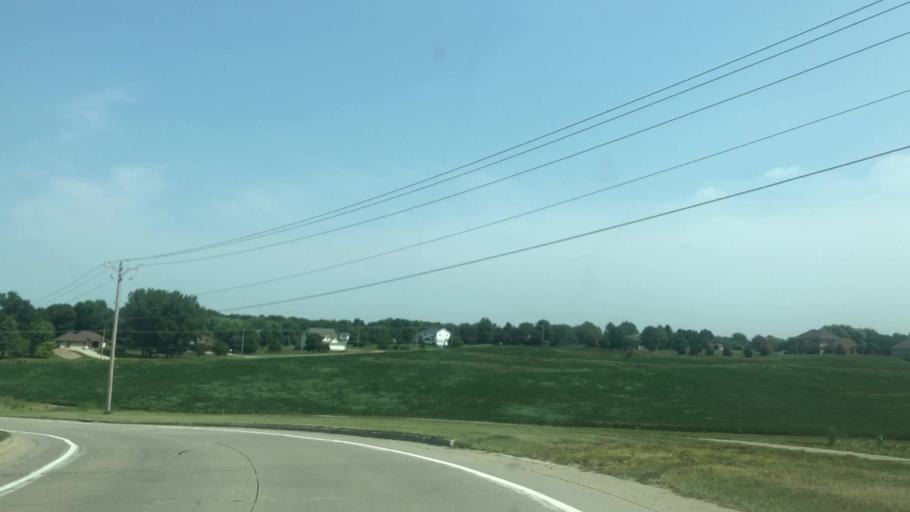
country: US
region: Iowa
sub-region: Marshall County
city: Marshalltown
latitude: 42.0182
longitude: -92.9461
